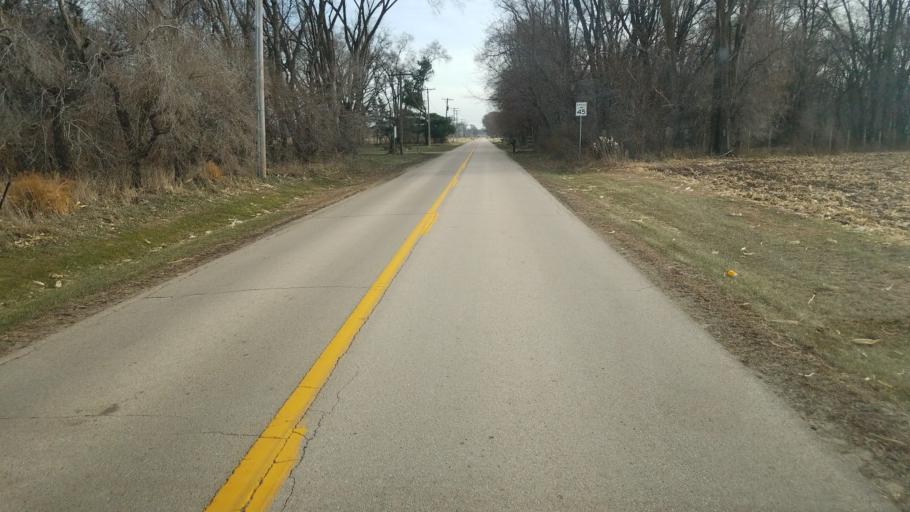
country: US
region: Illinois
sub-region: McHenry County
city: Marengo
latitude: 42.2378
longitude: -88.6516
